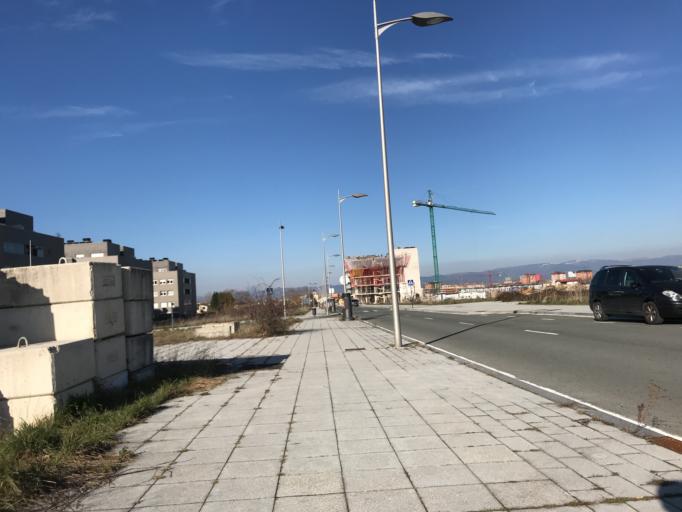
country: ES
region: Basque Country
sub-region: Provincia de Alava
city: Gasteiz / Vitoria
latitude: 42.8251
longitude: -2.6756
